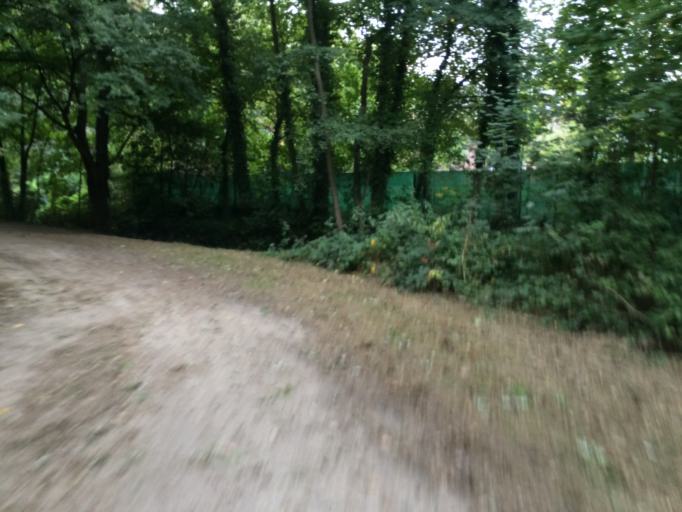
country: FR
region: Ile-de-France
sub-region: Departement de l'Essonne
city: Marcoussis
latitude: 48.6369
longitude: 2.2479
